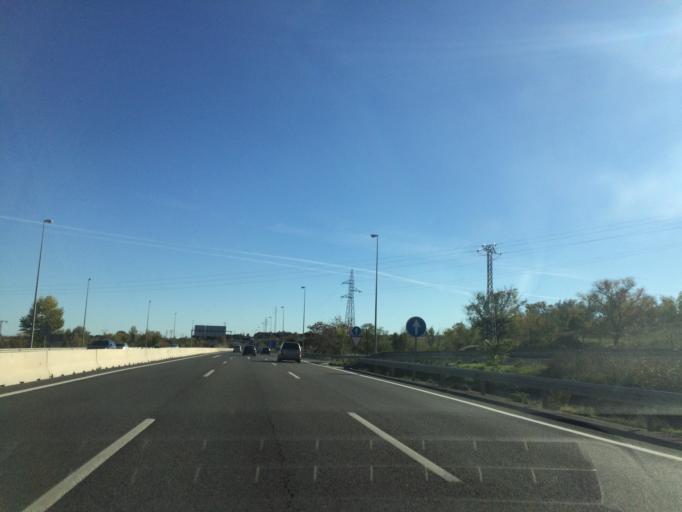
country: ES
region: Madrid
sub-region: Provincia de Madrid
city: Las Tablas
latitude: 40.5479
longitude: -3.7047
